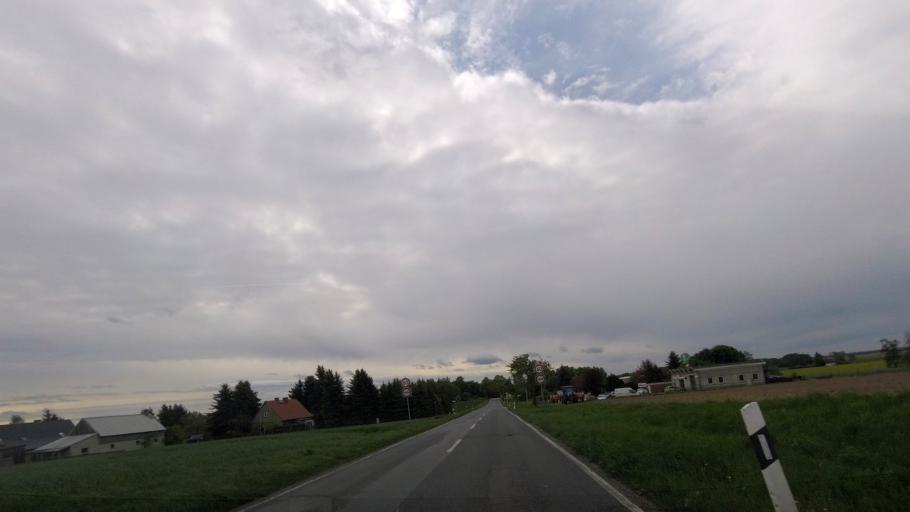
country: DE
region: Brandenburg
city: Dahme
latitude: 51.9060
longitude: 13.4057
